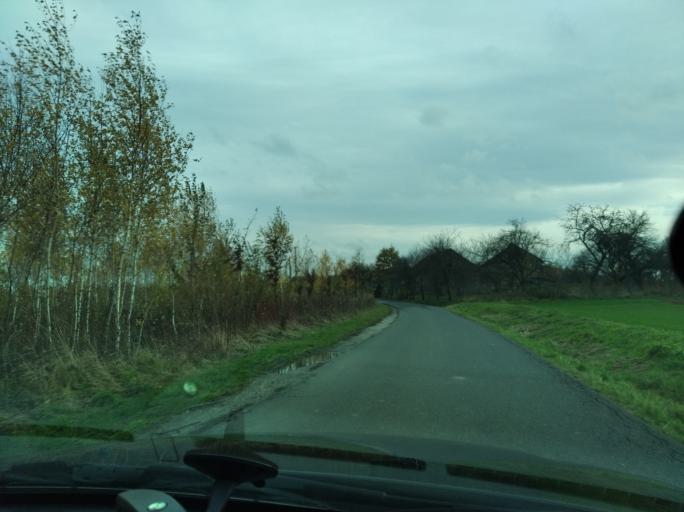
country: PL
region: Subcarpathian Voivodeship
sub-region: Powiat strzyzowski
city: Strzyzow
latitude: 49.9159
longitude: 21.7659
